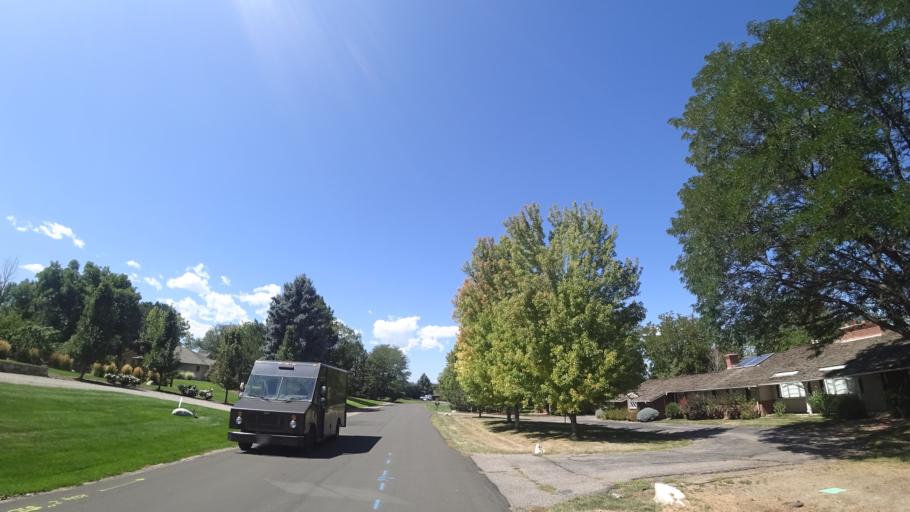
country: US
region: Colorado
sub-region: Arapahoe County
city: Cherry Hills Village
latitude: 39.6333
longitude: -104.9529
